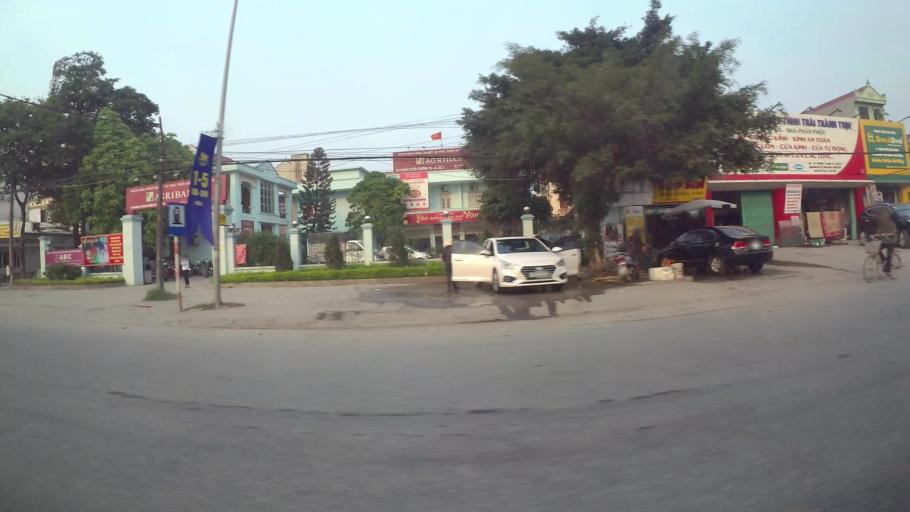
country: VN
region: Ha Noi
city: Thuong Tin
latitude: 20.8731
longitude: 105.8636
